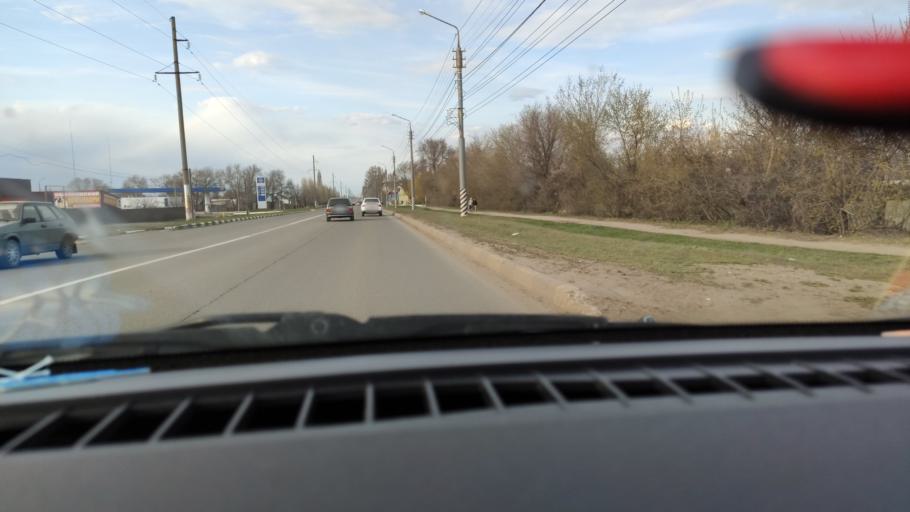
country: RU
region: Saratov
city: Privolzhskiy
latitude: 51.4030
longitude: 46.0377
